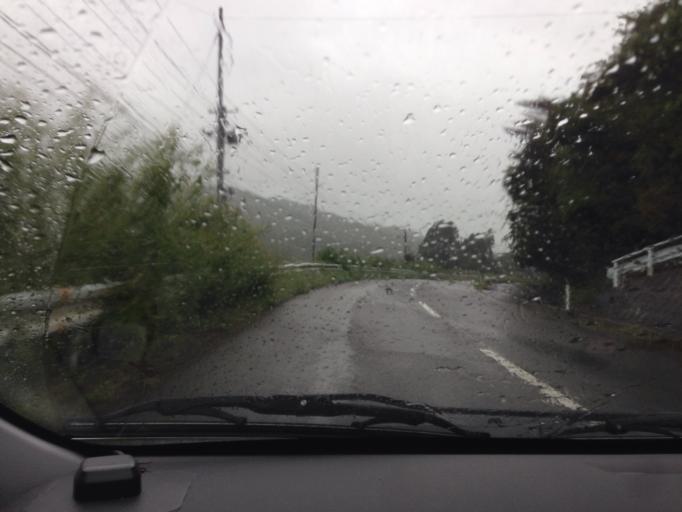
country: JP
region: Fukushima
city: Koriyama
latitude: 37.4286
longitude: 140.2687
